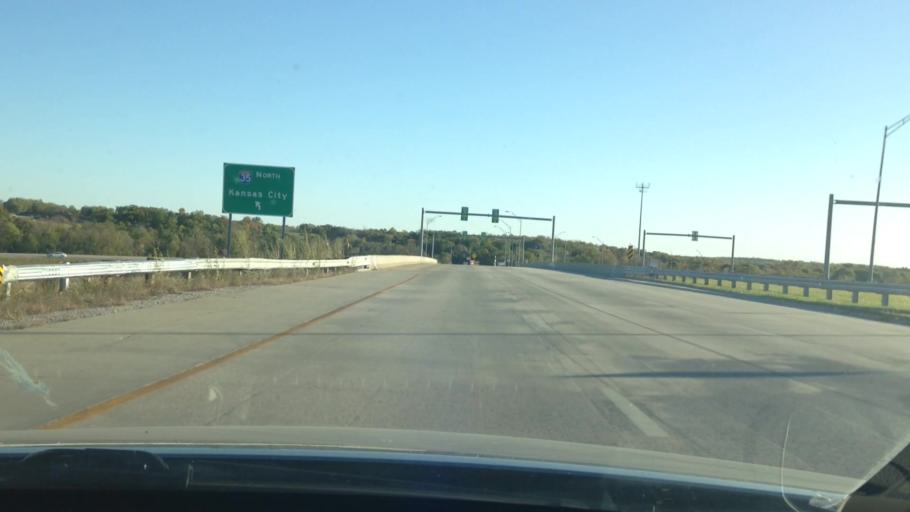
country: US
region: Kansas
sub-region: Johnson County
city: Edgerton
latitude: 38.7605
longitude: -94.9639
